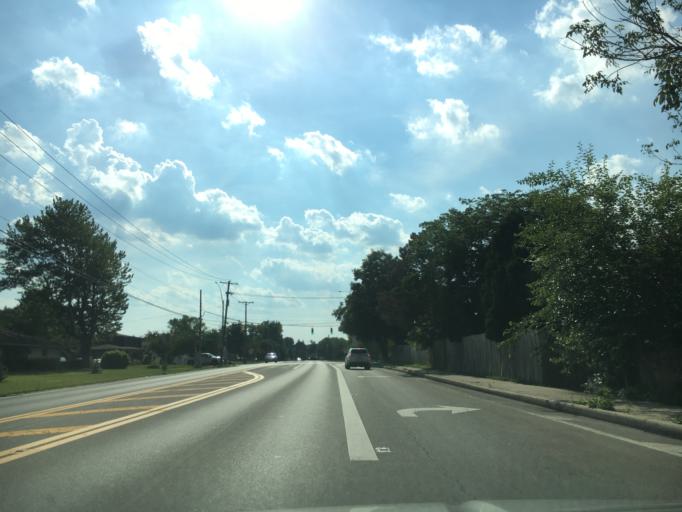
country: US
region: Ohio
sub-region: Franklin County
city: Lincoln Village
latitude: 39.9828
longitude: -83.1640
